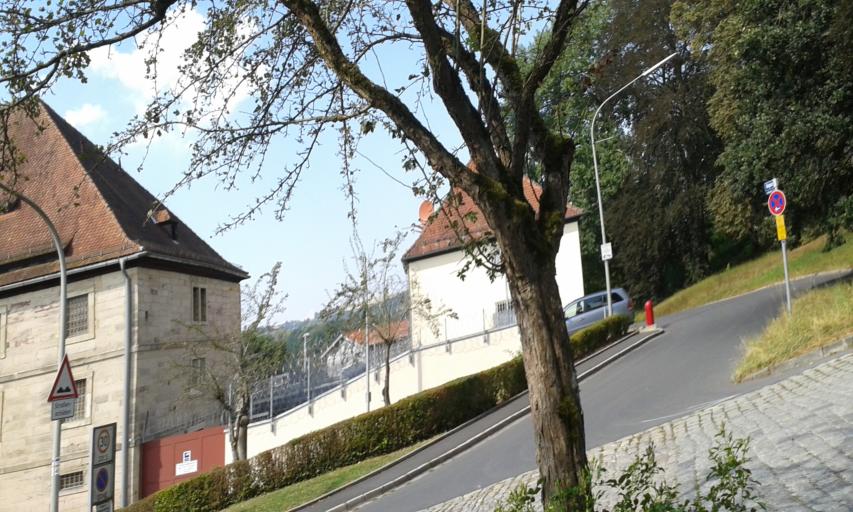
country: DE
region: Bavaria
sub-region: Upper Franconia
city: Kronach
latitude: 50.2434
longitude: 11.3267
